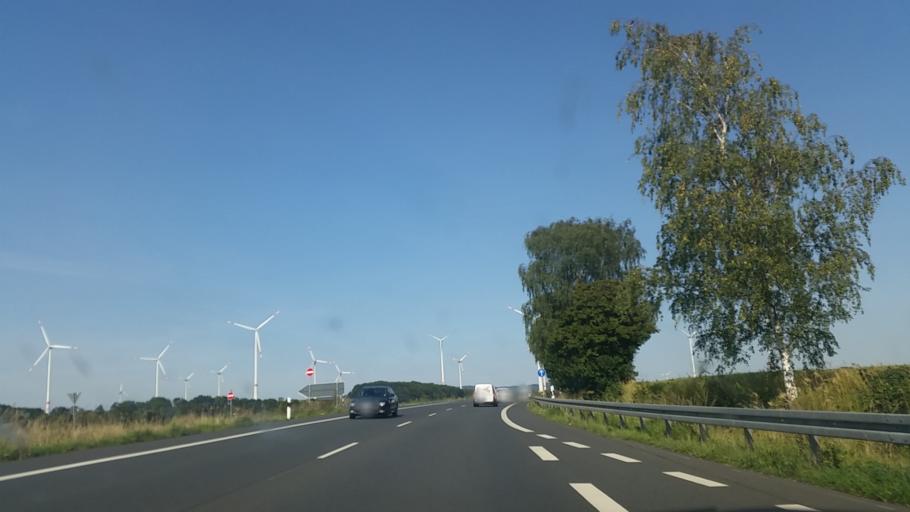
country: DE
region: Lower Saxony
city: Coppenbrugge
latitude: 52.1109
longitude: 9.4876
